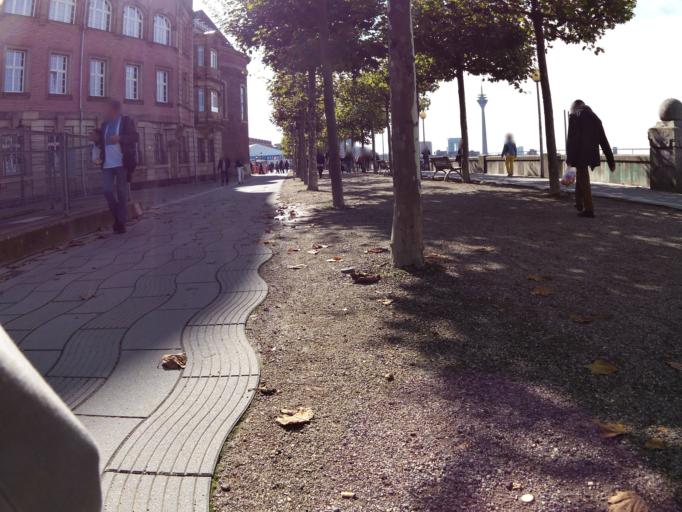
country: DE
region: North Rhine-Westphalia
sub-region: Regierungsbezirk Dusseldorf
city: Dusseldorf
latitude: 51.2291
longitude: 6.7710
